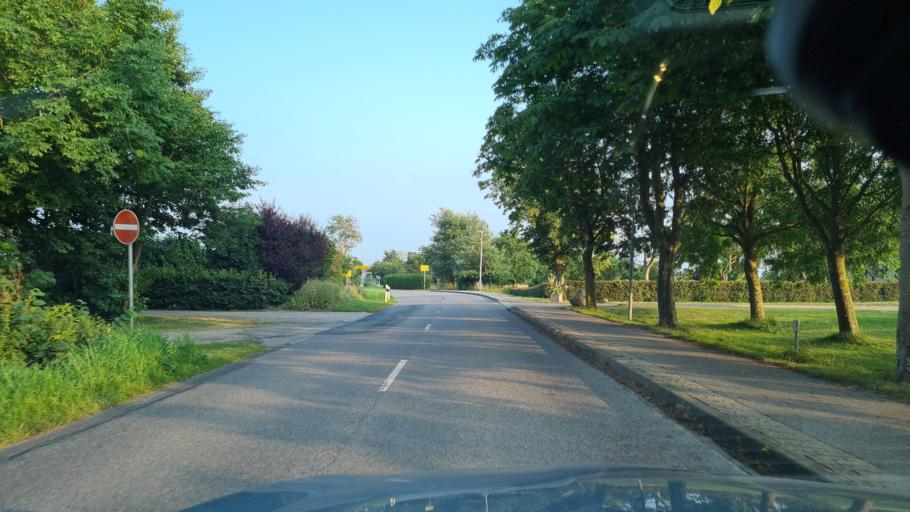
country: DE
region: Schleswig-Holstein
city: Elisabeth-Sophien-Koog
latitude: 54.4894
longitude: 8.8479
